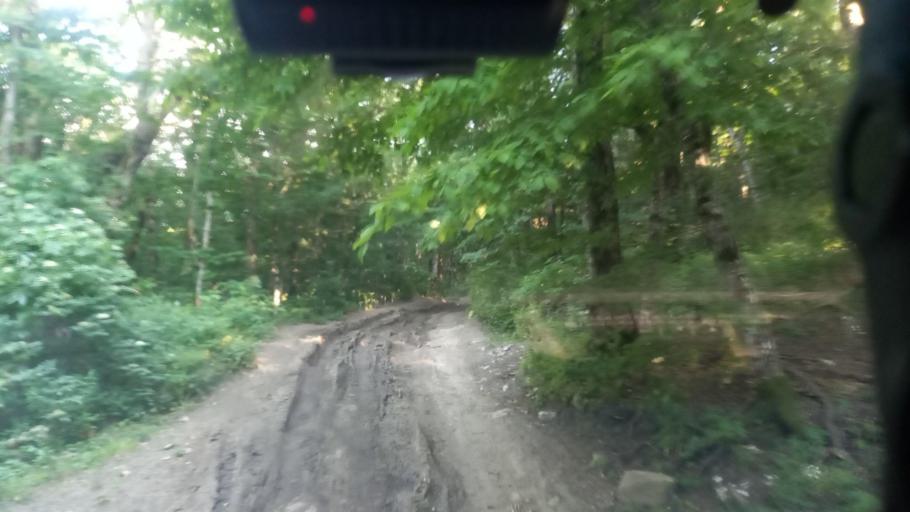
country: RU
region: Krasnodarskiy
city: Gelendzhik
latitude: 44.6214
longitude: 38.1879
